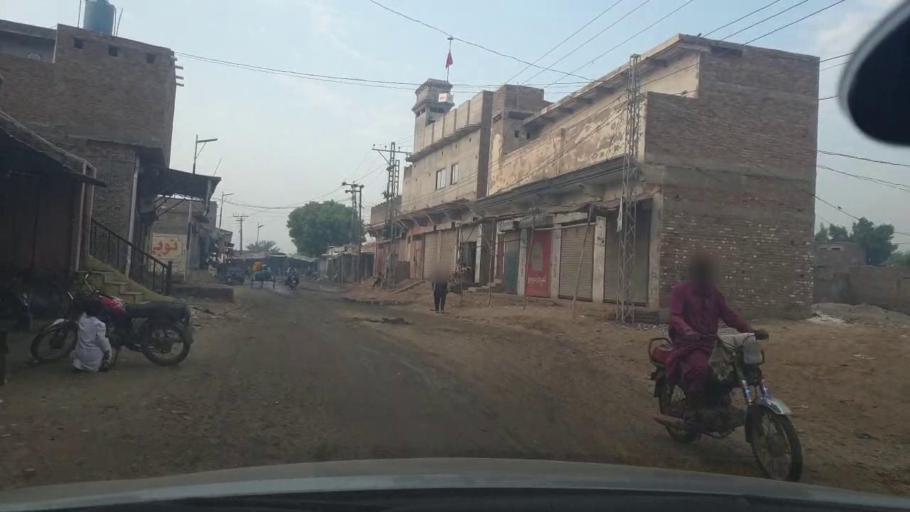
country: PK
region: Sindh
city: Jacobabad
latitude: 28.2805
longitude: 68.4256
